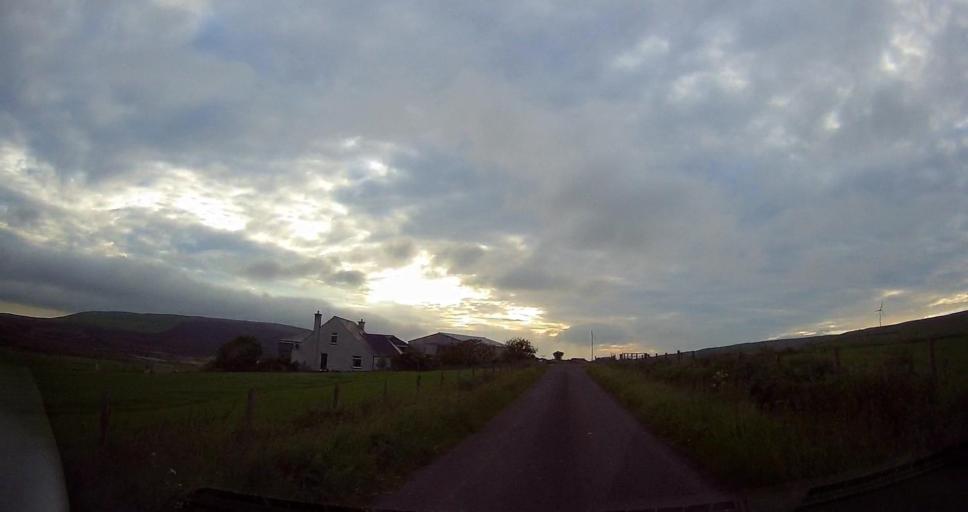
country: GB
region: Scotland
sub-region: Orkney Islands
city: Stromness
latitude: 59.0941
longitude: -3.1869
